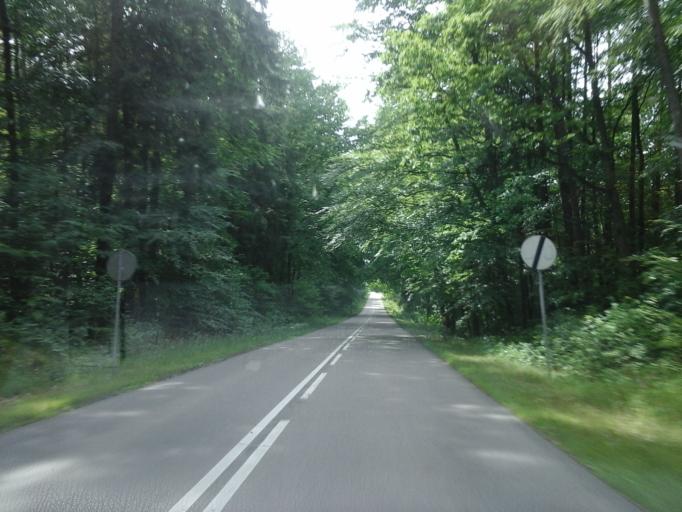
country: PL
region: West Pomeranian Voivodeship
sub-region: Powiat lobeski
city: Lobez
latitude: 53.5970
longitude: 15.6137
